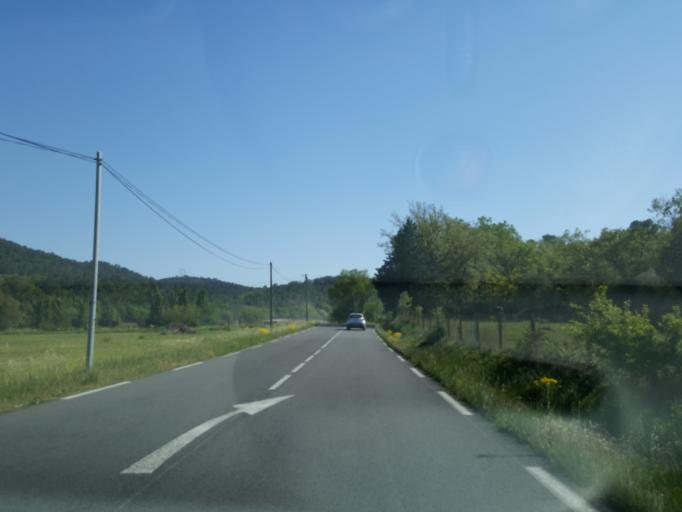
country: FR
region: Provence-Alpes-Cote d'Azur
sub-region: Departement du Var
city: Neoules
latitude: 43.3080
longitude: 5.9883
